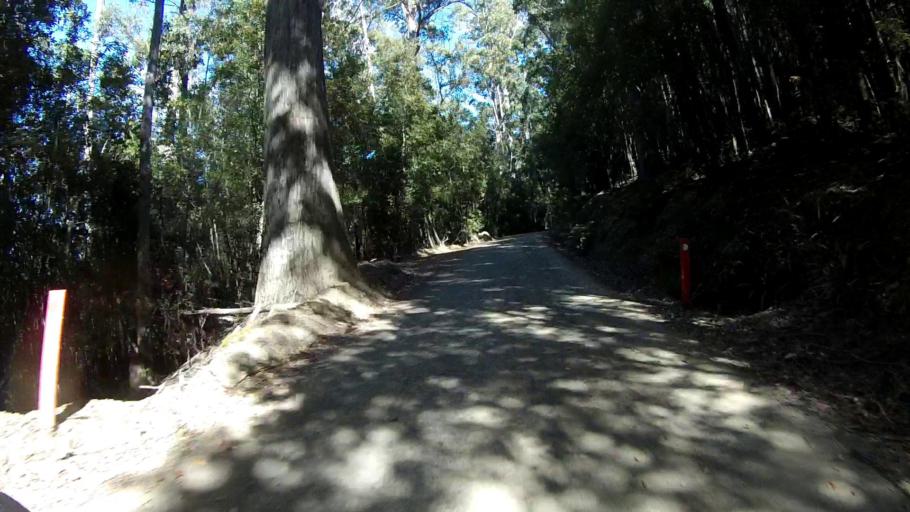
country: AU
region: Tasmania
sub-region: Derwent Valley
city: New Norfolk
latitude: -42.6762
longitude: 146.6976
